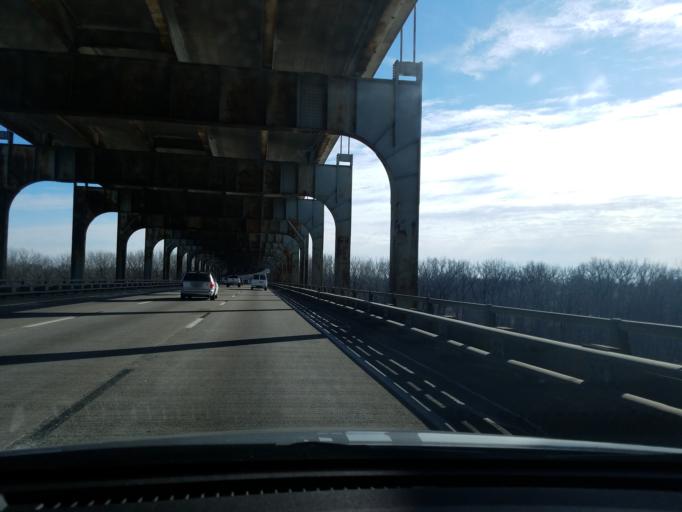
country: US
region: Indiana
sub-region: Floyd County
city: New Albany
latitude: 38.2780
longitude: -85.8215
